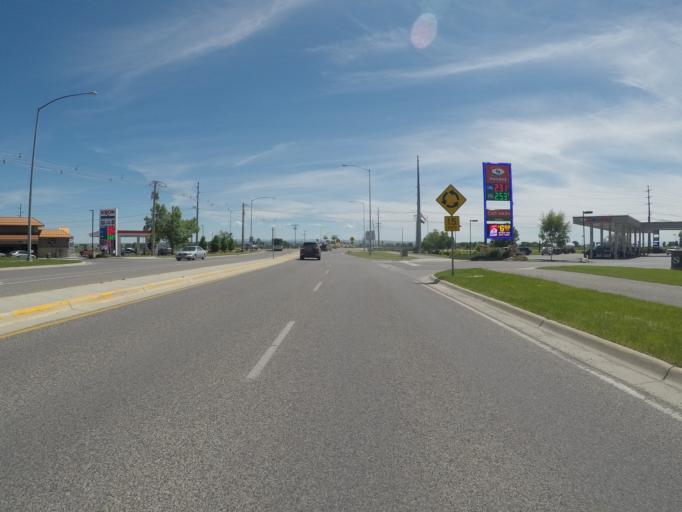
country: US
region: Montana
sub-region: Yellowstone County
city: Billings
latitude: 45.7855
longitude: -108.6178
